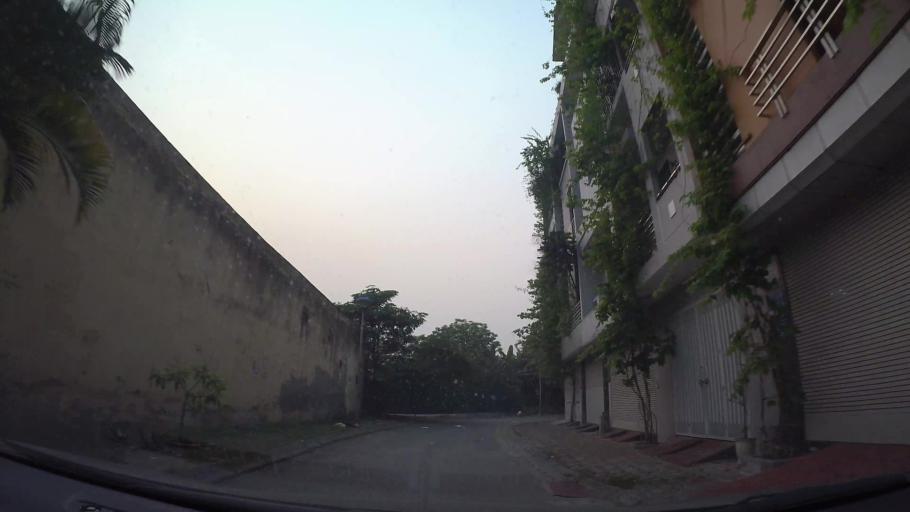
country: VN
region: Ha Noi
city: Thanh Xuan
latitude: 20.9775
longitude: 105.7955
